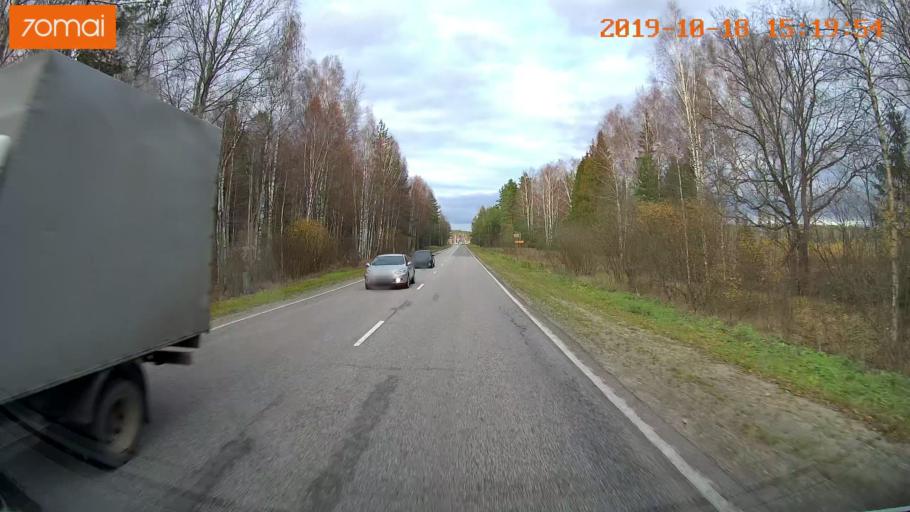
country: RU
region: Vladimir
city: Anopino
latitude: 55.6798
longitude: 40.7411
